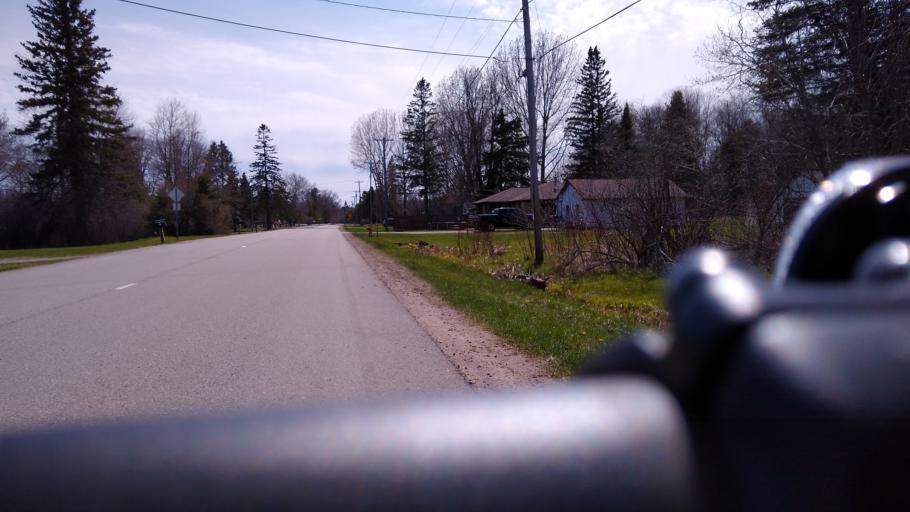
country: US
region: Michigan
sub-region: Delta County
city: Escanaba
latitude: 45.6792
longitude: -87.1448
